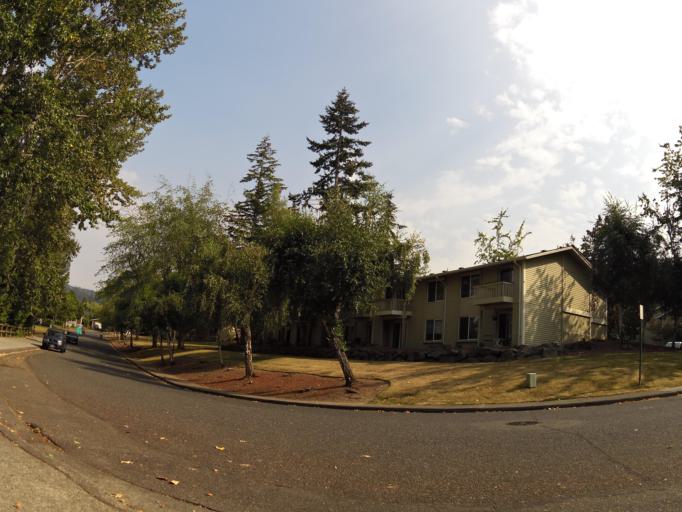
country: US
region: Washington
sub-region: Whatcom County
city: Bellingham
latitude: 48.7151
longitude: -122.4940
